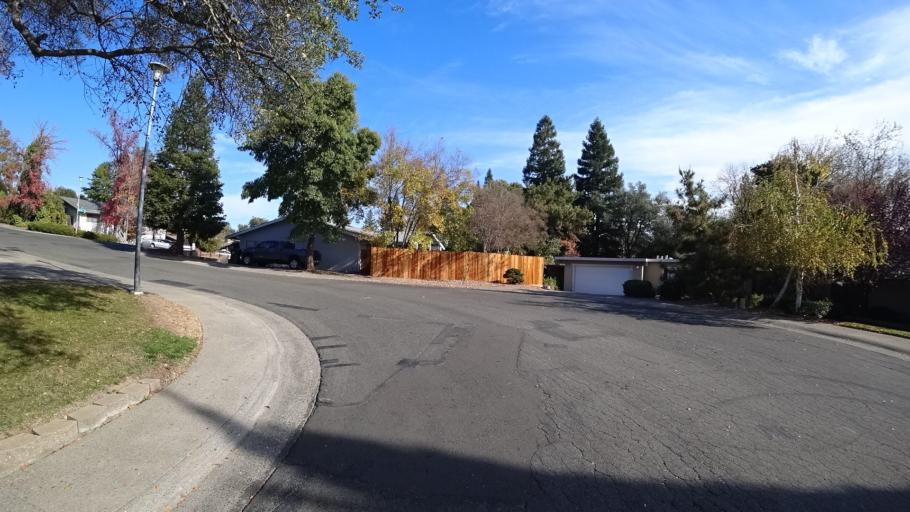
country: US
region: California
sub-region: Sacramento County
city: Fair Oaks
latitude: 38.6681
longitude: -121.2824
